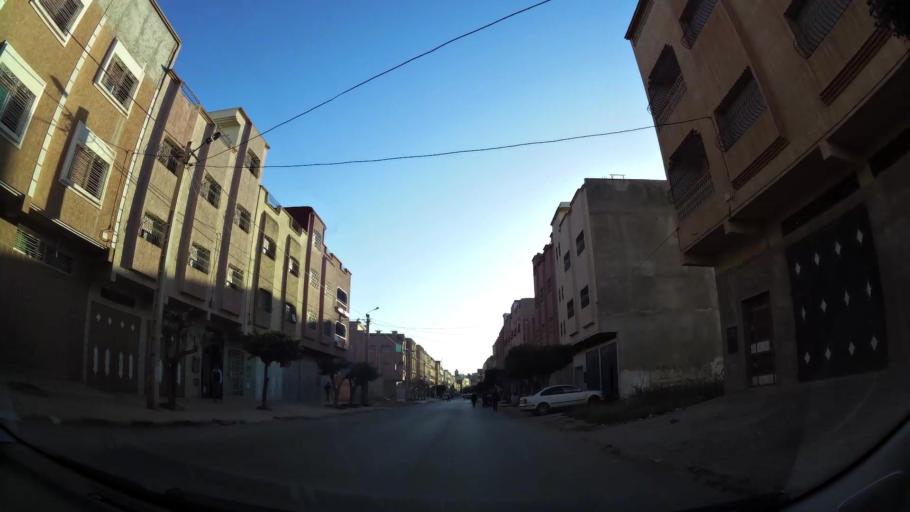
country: MA
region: Oriental
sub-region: Berkane-Taourirt
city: Berkane
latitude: 34.9249
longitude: -2.3157
